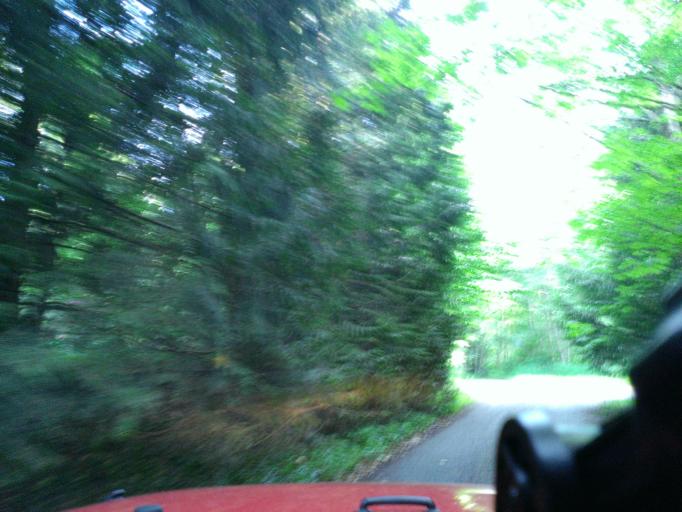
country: US
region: Washington
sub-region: King County
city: Union Hill-Novelty Hill
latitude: 47.6713
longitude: -122.0170
